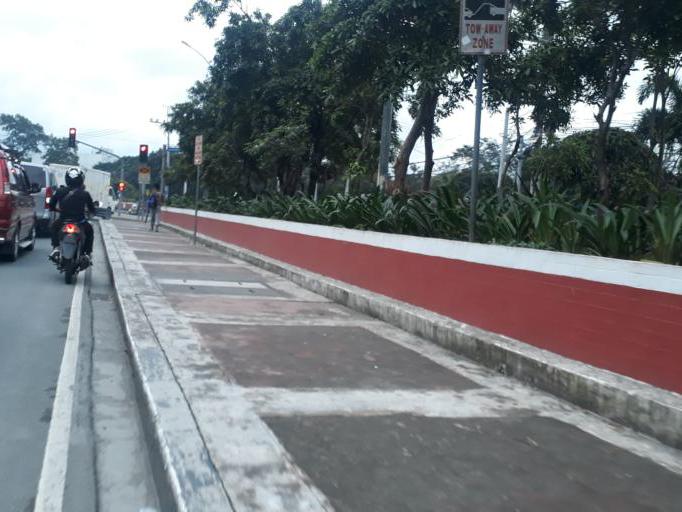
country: PH
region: Calabarzon
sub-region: Province of Rizal
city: San Mateo
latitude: 14.6910
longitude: 121.0958
